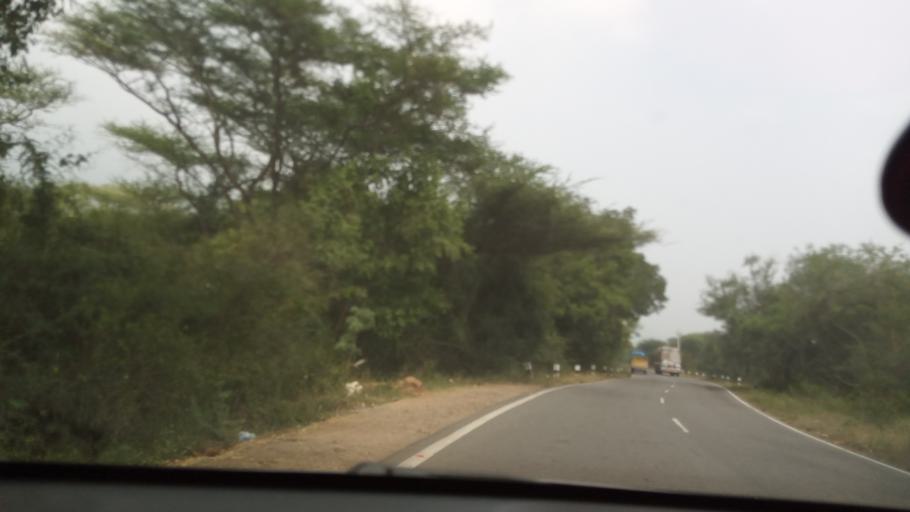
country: IN
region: Tamil Nadu
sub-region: Erode
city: Sathyamangalam
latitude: 11.5681
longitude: 77.1350
